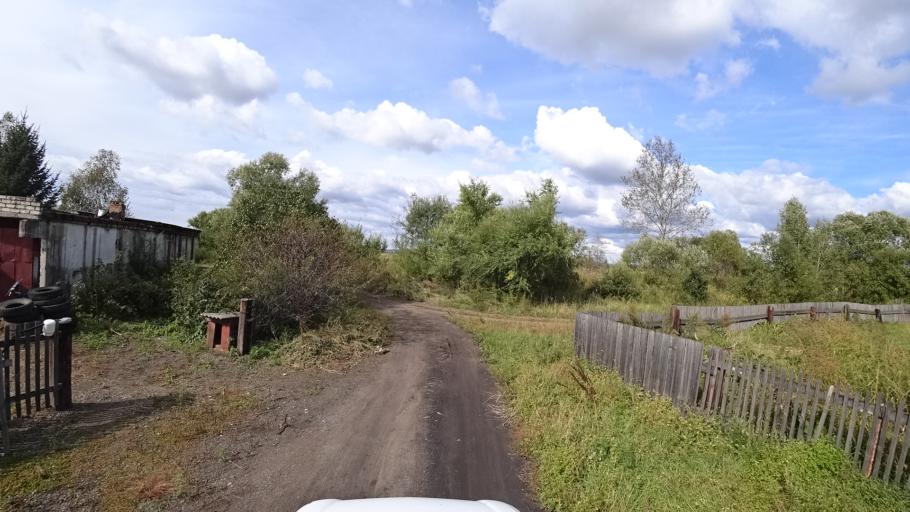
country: RU
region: Amur
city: Arkhara
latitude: 49.3539
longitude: 130.1581
